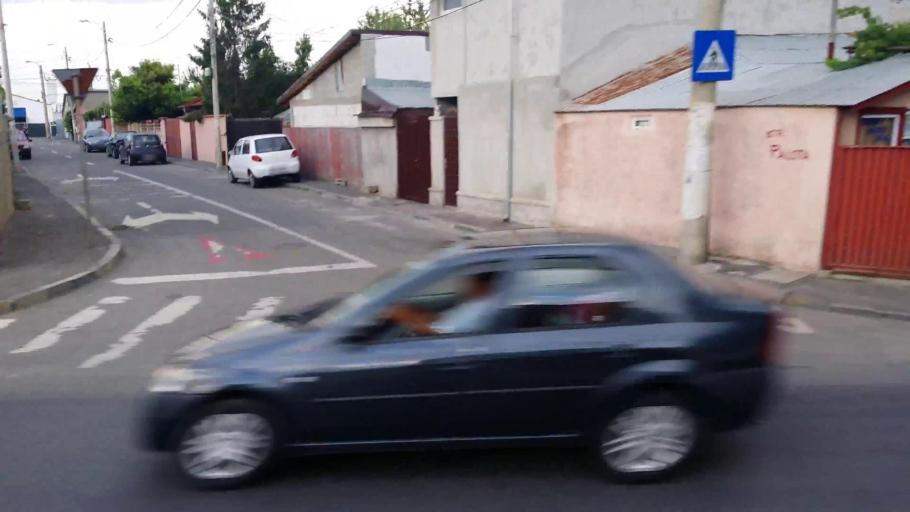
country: RO
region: Bucuresti
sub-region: Municipiul Bucuresti
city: Bucuresti
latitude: 44.3827
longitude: 26.0830
